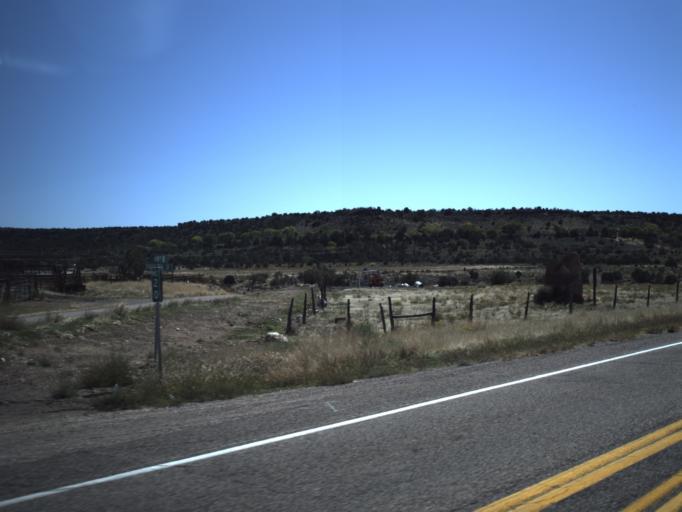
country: US
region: Utah
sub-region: Washington County
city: Ivins
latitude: 37.3358
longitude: -113.6933
